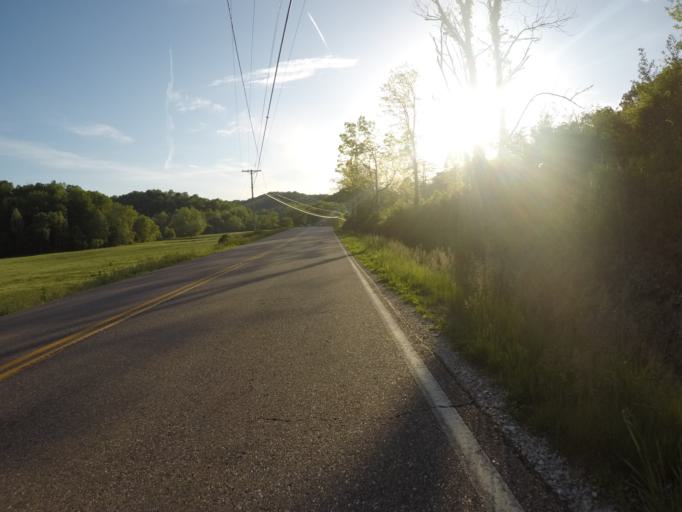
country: US
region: West Virginia
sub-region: Cabell County
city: Huntington
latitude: 38.5543
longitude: -82.4594
